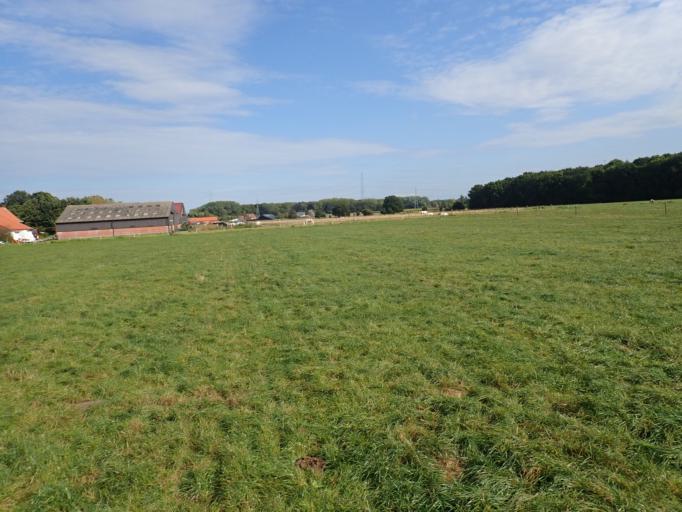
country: BE
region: Flanders
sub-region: Provincie Antwerpen
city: Lint
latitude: 51.1375
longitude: 4.5026
